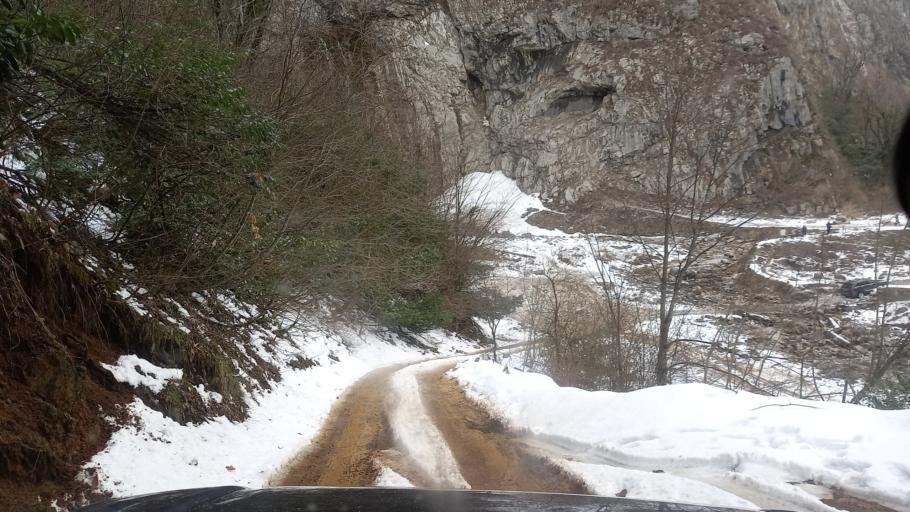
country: GE
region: Abkhazia
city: Gagra
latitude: 43.4344
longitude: 40.4430
